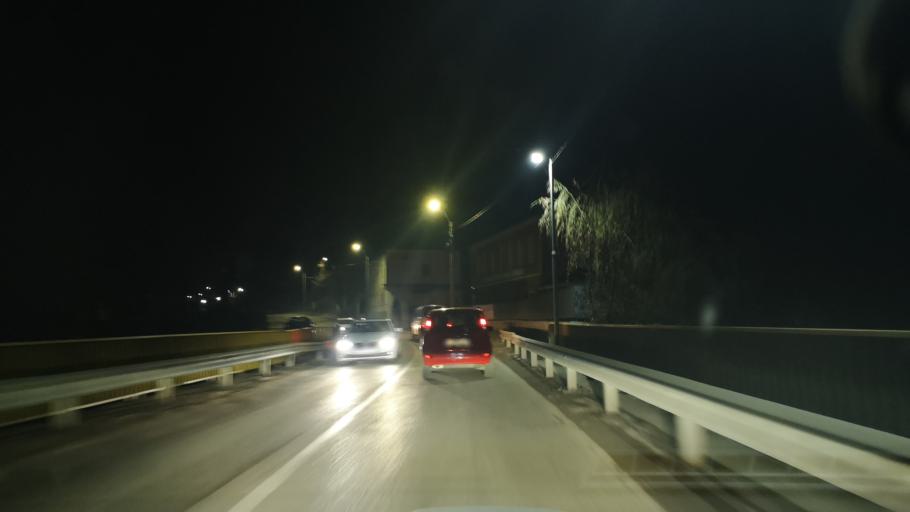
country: MD
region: Orhei
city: Orhei
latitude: 47.3661
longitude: 28.8128
